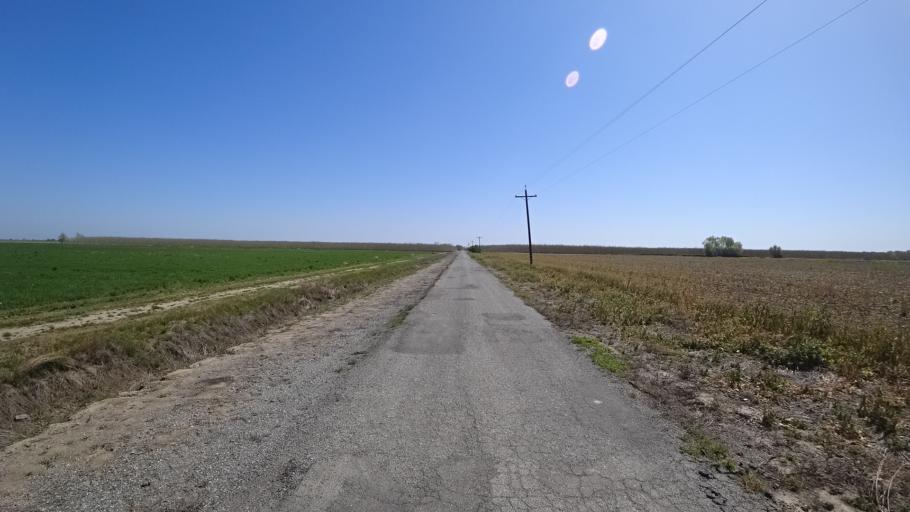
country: US
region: California
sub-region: Glenn County
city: Willows
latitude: 39.4990
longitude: -122.0363
